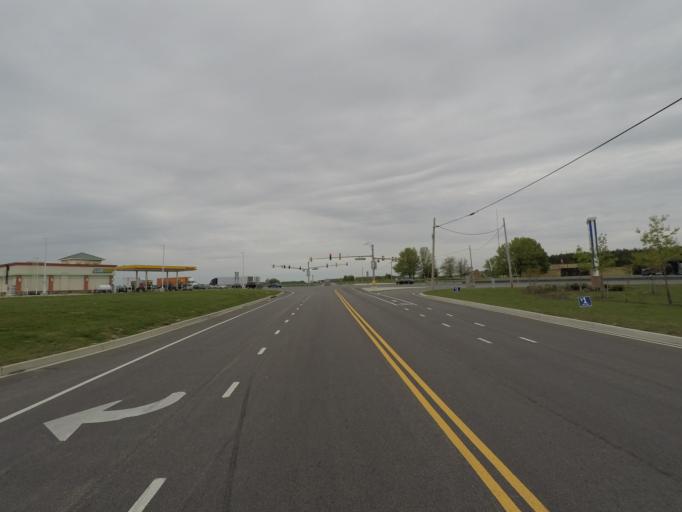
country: US
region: Maryland
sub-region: Caroline County
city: Ridgely
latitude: 38.9231
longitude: -75.9576
